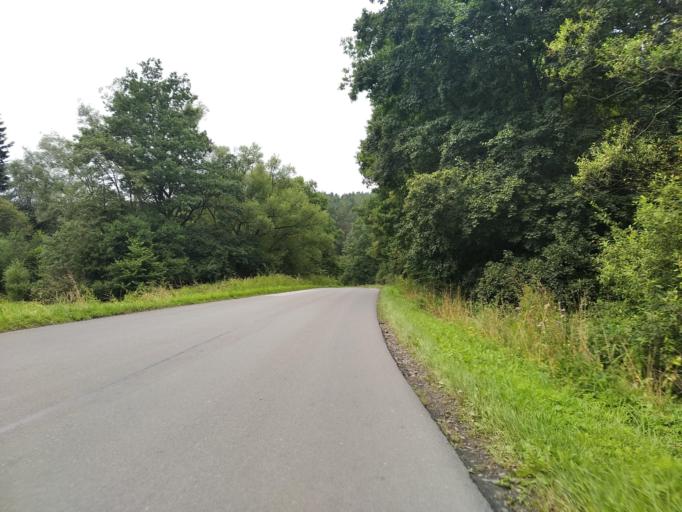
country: PL
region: Subcarpathian Voivodeship
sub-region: Powiat przemyski
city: Bircza
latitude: 49.6927
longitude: 22.4305
